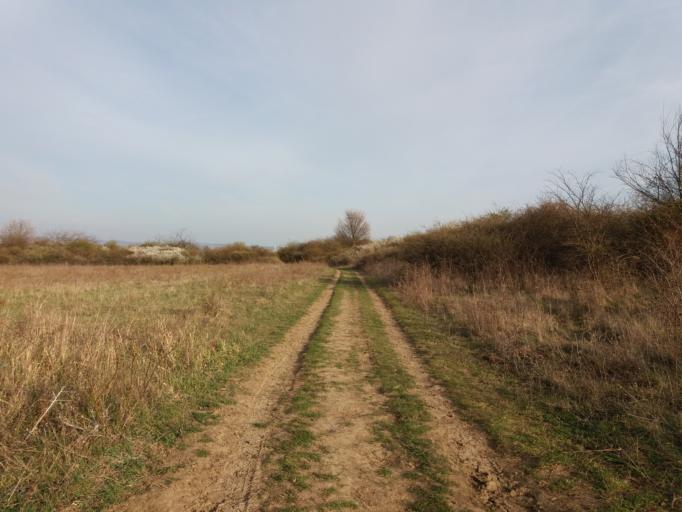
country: HU
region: Pest
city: Pomaz
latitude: 47.6245
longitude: 19.0205
